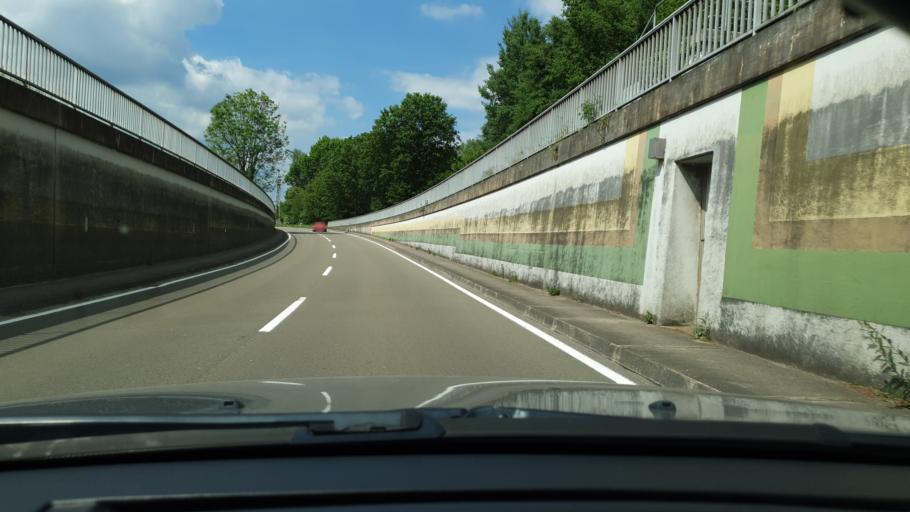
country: DE
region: Rheinland-Pfalz
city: Hauptstuhl
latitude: 49.4023
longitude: 7.4929
